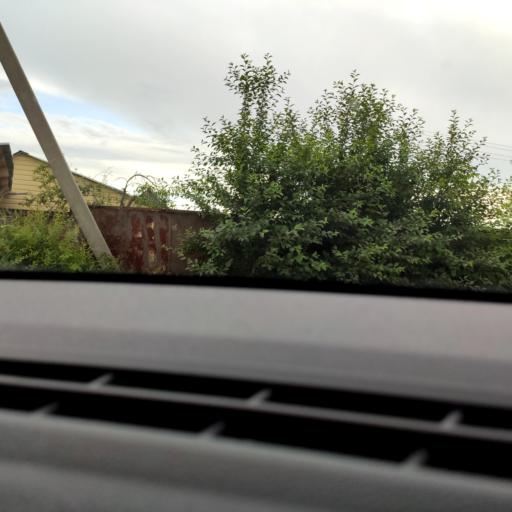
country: RU
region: Samara
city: Podstepki
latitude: 53.5115
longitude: 49.0757
